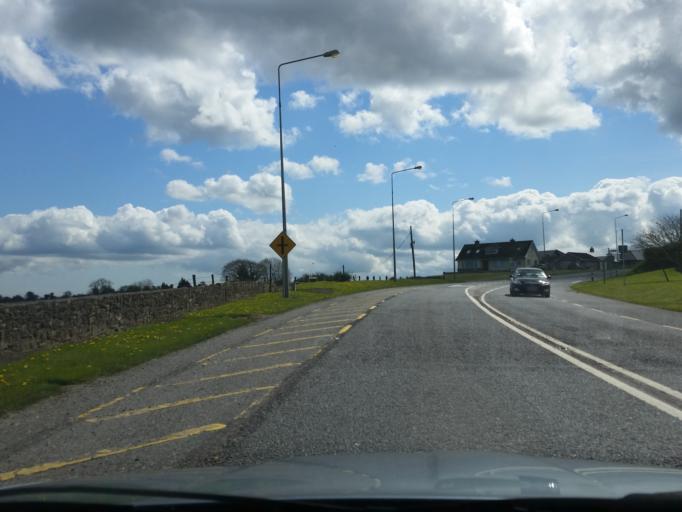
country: IE
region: Leinster
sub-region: An Mhi
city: Slane
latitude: 53.7005
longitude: -6.5387
